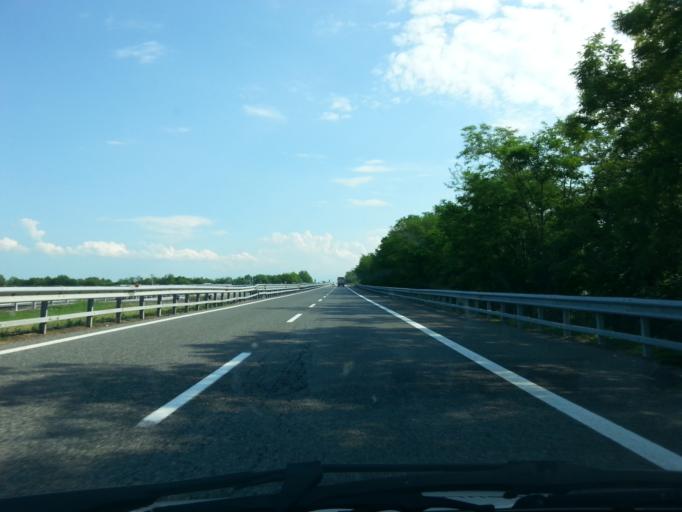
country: IT
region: Piedmont
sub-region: Provincia di Cuneo
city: Caramagna Piemonte
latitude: 44.8034
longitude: 7.7520
